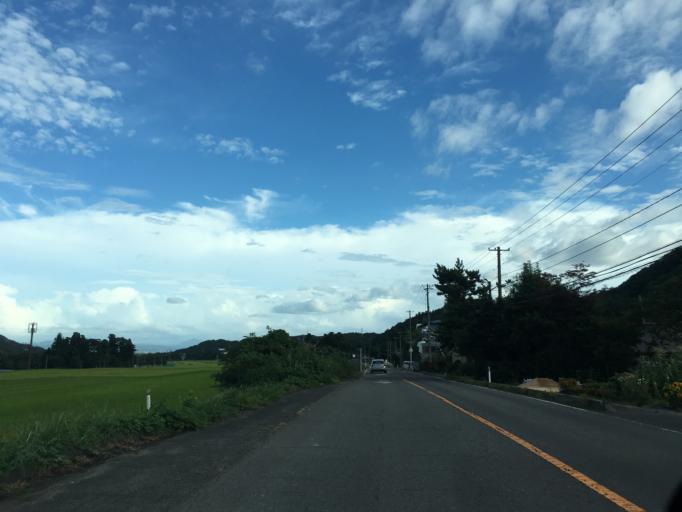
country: JP
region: Fukushima
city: Motomiya
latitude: 37.5037
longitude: 140.2757
